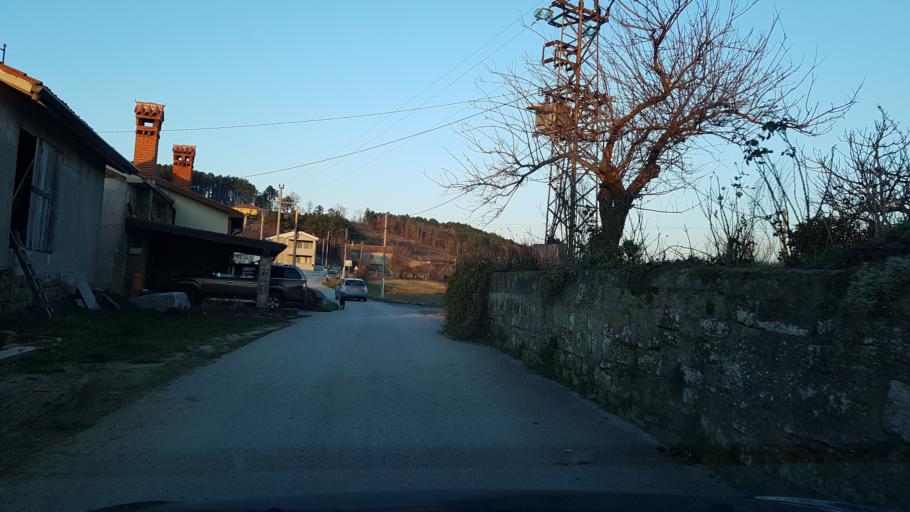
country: SI
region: Koper-Capodistria
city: Sv. Anton
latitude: 45.4986
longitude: 13.8552
